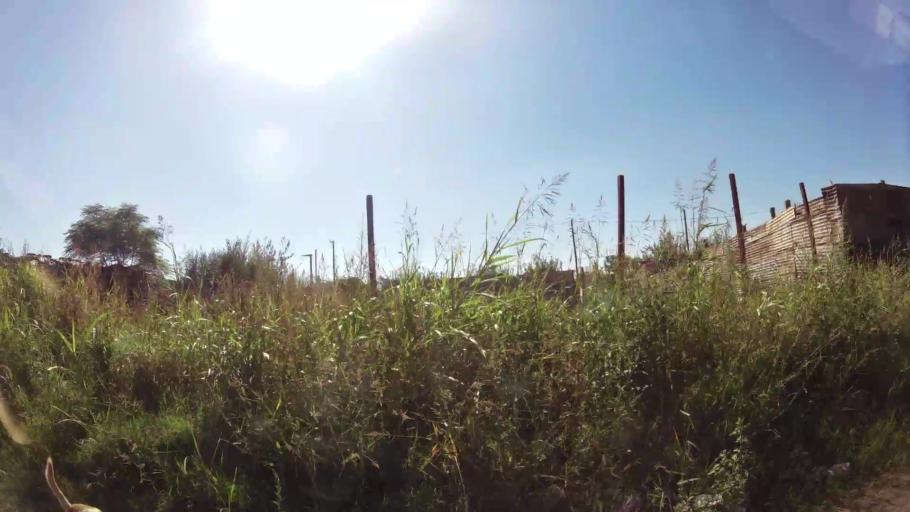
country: AR
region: Cordoba
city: Villa Allende
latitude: -31.3267
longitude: -64.2445
